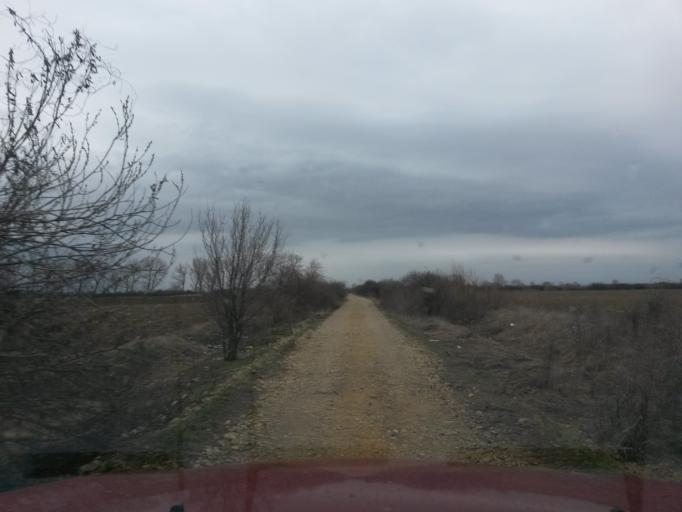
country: SK
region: Kosicky
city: Michalovce
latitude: 48.6927
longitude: 21.8977
